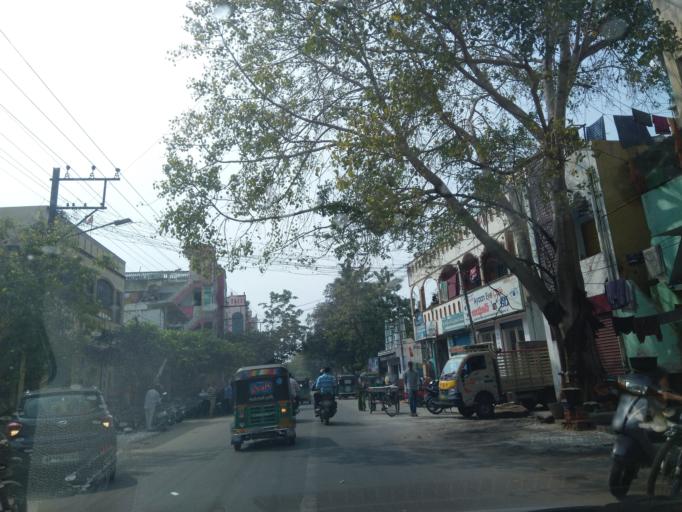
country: IN
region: Andhra Pradesh
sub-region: Krishna
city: Vijayawada
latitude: 16.5226
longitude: 80.6037
